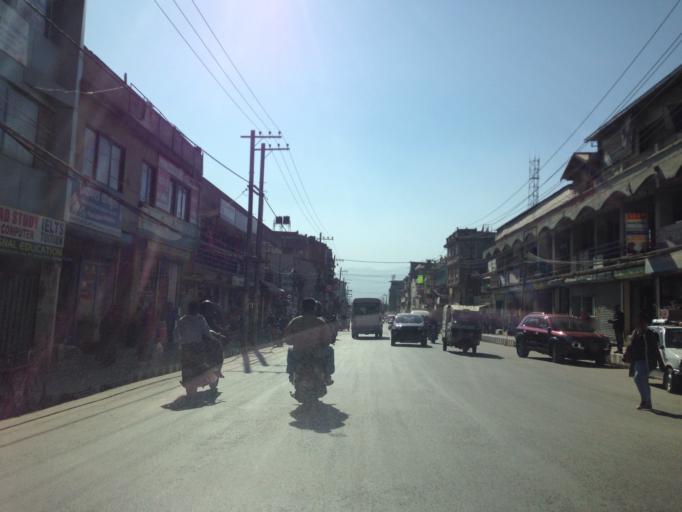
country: NP
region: Central Region
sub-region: Bagmati Zone
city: Kathmandu
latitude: 27.7416
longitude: 85.3385
